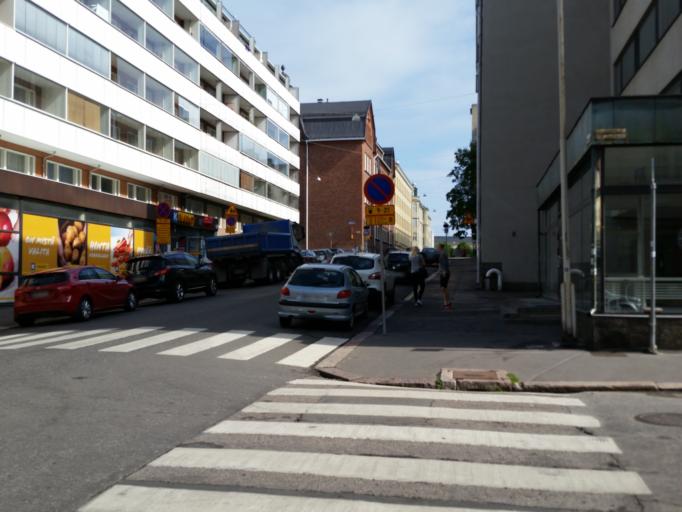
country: FI
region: Uusimaa
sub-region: Helsinki
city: Helsinki
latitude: 60.1617
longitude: 24.9369
